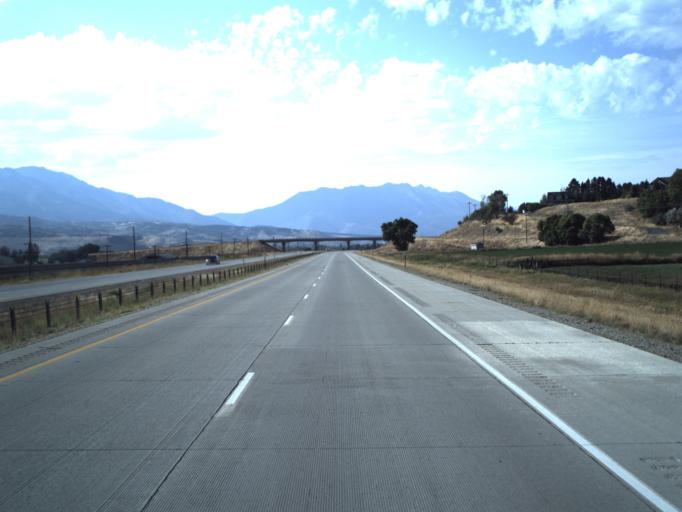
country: US
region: Utah
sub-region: Morgan County
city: Morgan
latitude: 41.0628
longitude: -111.7060
